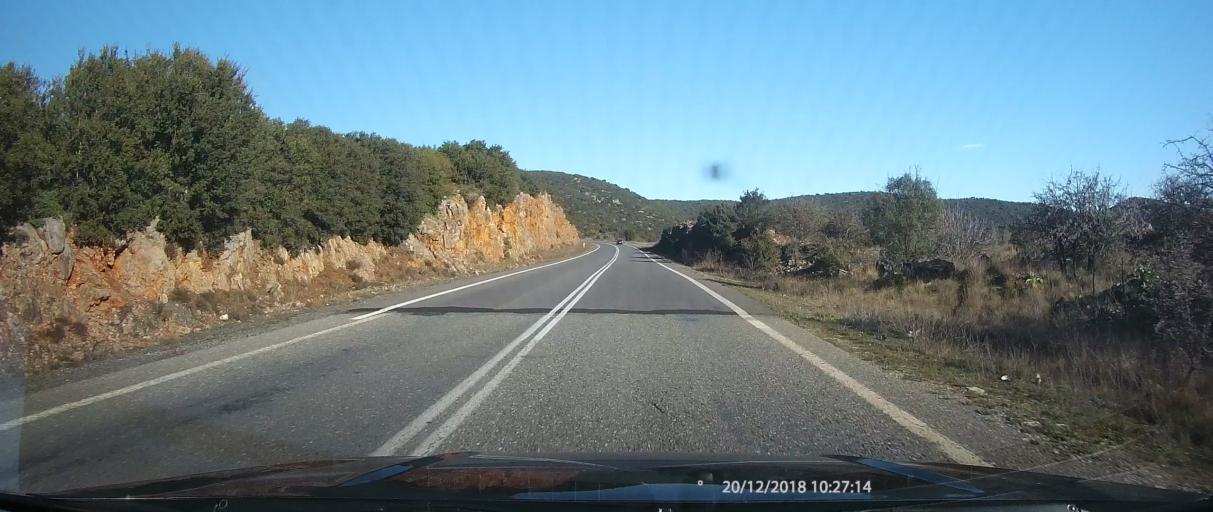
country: GR
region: Peloponnese
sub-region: Nomos Lakonias
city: Kariai
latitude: 37.2416
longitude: 22.4403
